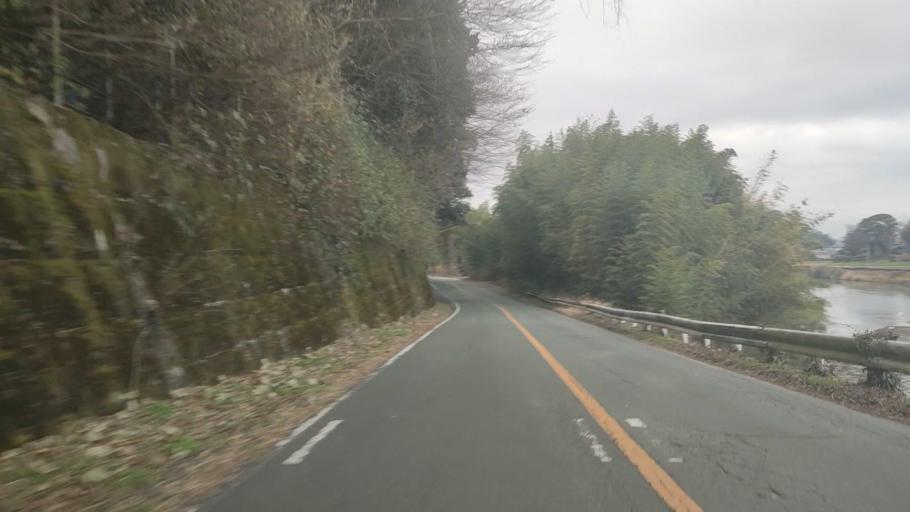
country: JP
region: Kumamoto
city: Ozu
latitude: 32.8530
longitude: 130.8656
